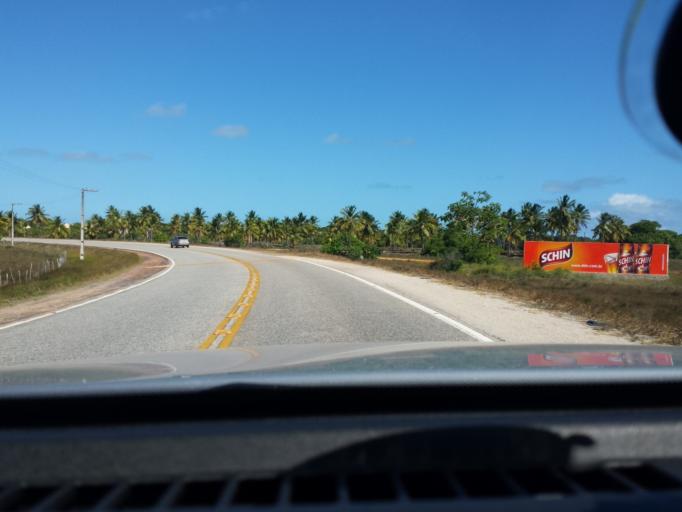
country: BR
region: Sergipe
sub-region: Estancia
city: Estancia
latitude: -11.2656
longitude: -37.2666
